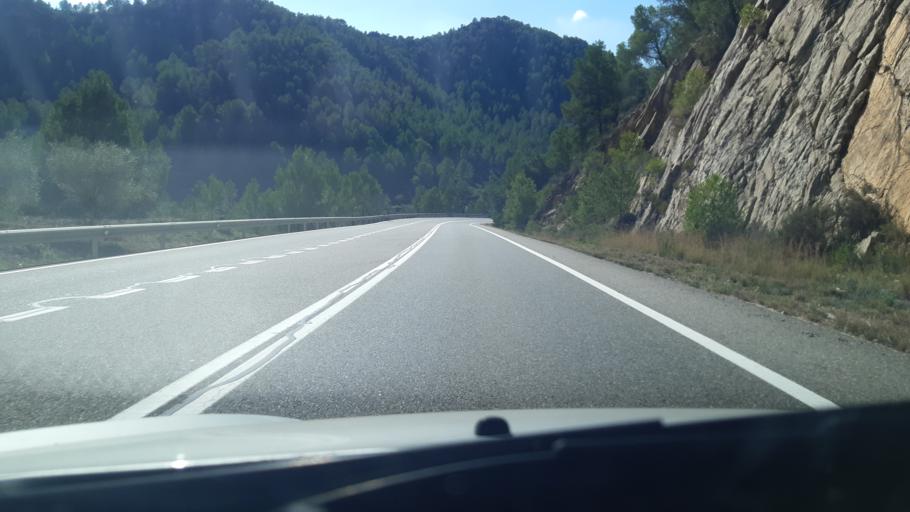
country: ES
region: Catalonia
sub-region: Provincia de Tarragona
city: Rasquera
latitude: 40.9961
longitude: 0.5724
